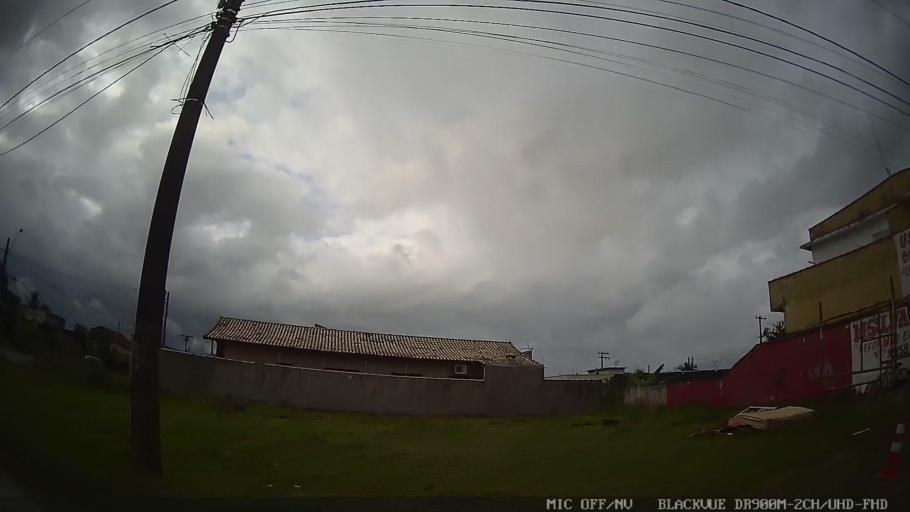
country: BR
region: Sao Paulo
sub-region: Itanhaem
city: Itanhaem
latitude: -24.2083
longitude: -46.8581
